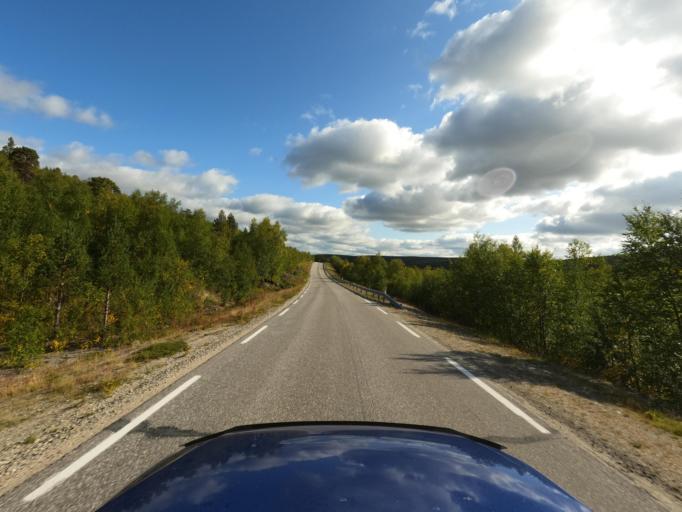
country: NO
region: Finnmark Fylke
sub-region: Porsanger
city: Lakselv
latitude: 69.4217
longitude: 24.8028
